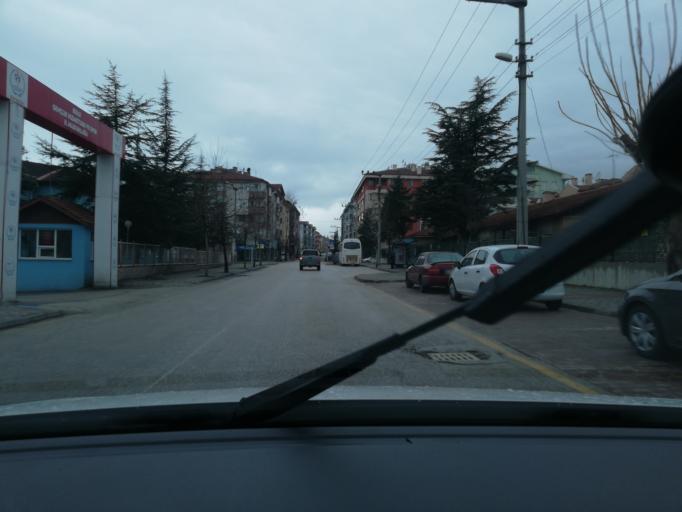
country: TR
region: Bolu
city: Bolu
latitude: 40.7375
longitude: 31.6065
